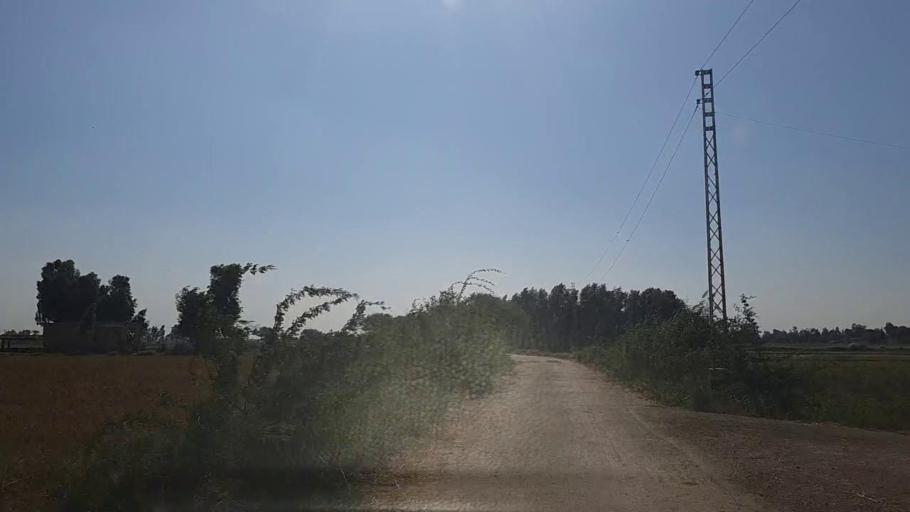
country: PK
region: Sindh
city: Thatta
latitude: 24.7739
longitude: 67.9476
